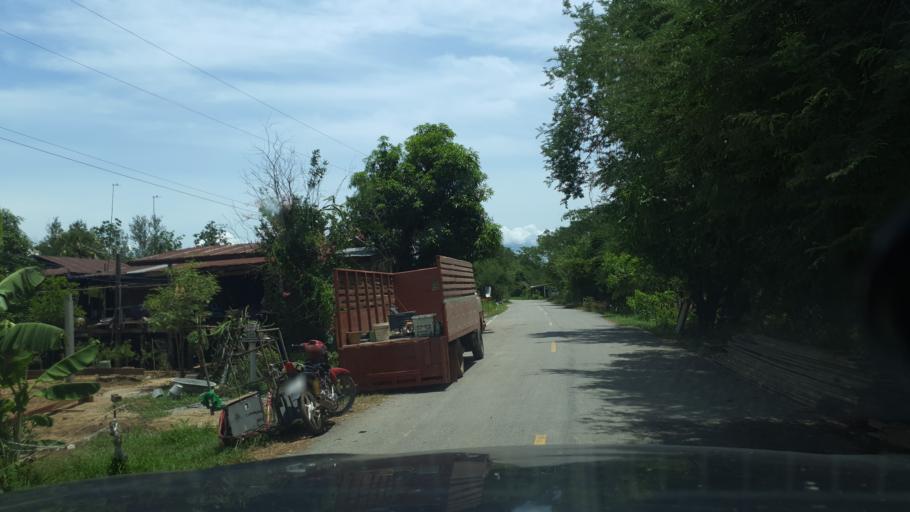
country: TH
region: Sukhothai
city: Ban Na
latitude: 17.1101
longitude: 99.6781
